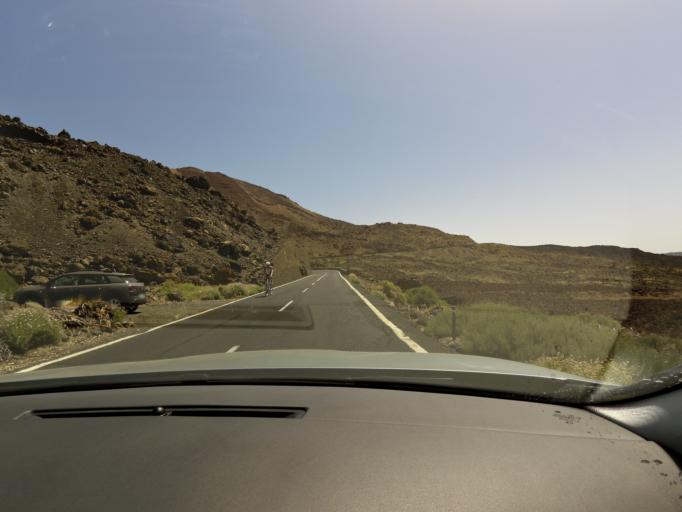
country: ES
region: Canary Islands
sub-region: Provincia de Santa Cruz de Tenerife
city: Vilaflor
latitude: 28.2558
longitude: -16.6190
